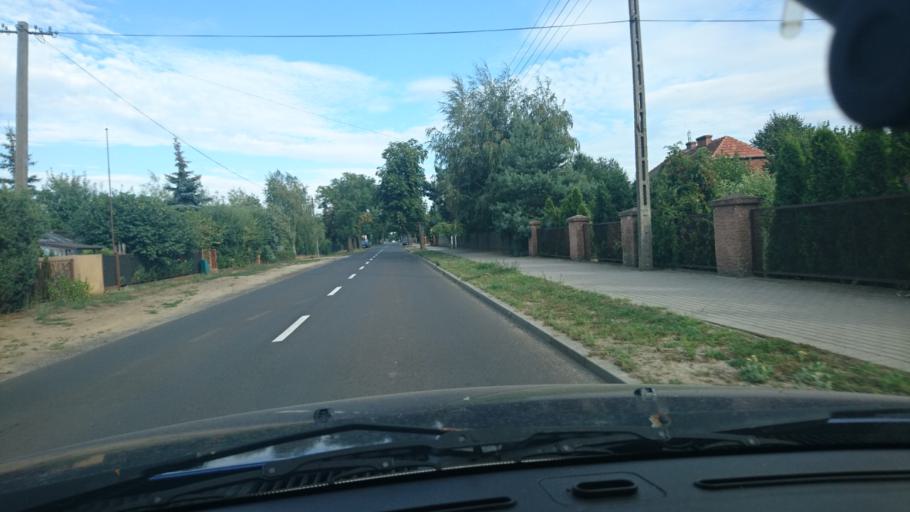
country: PL
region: Greater Poland Voivodeship
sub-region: Powiat ostrzeszowski
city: Ostrzeszow
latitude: 51.4302
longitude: 17.9146
